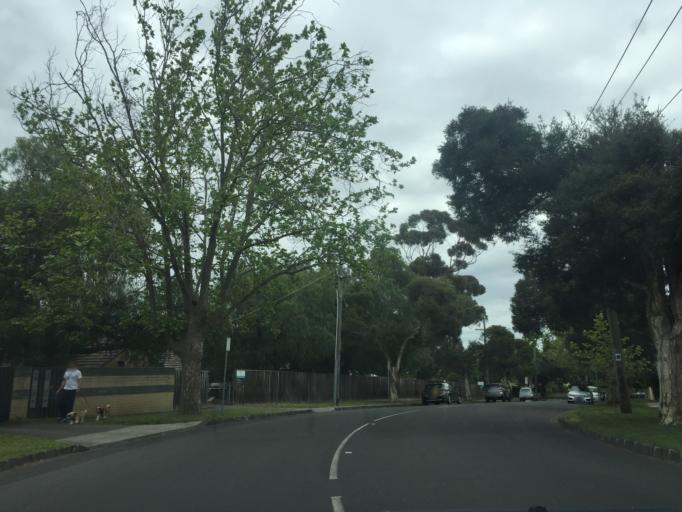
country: AU
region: Victoria
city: Balwyn
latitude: -37.8173
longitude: 145.0621
